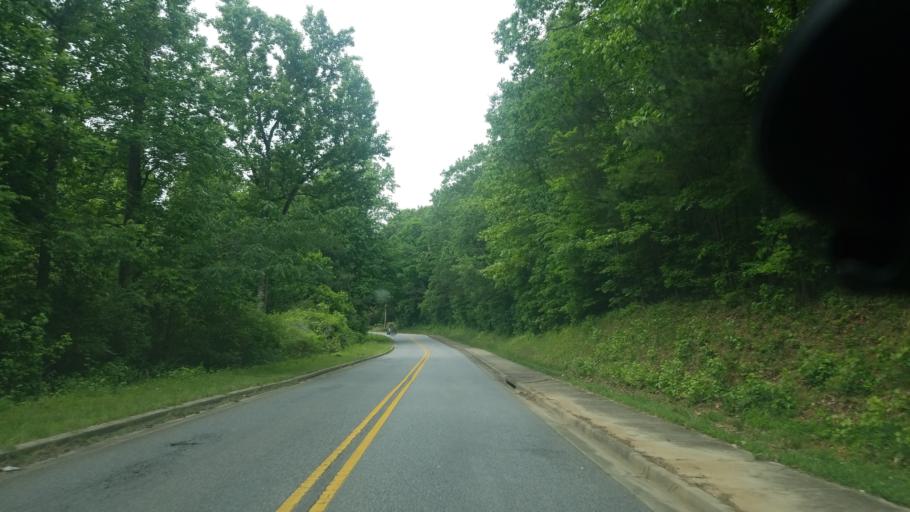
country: US
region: Georgia
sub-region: Forsyth County
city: Cumming
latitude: 34.1490
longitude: -84.1297
